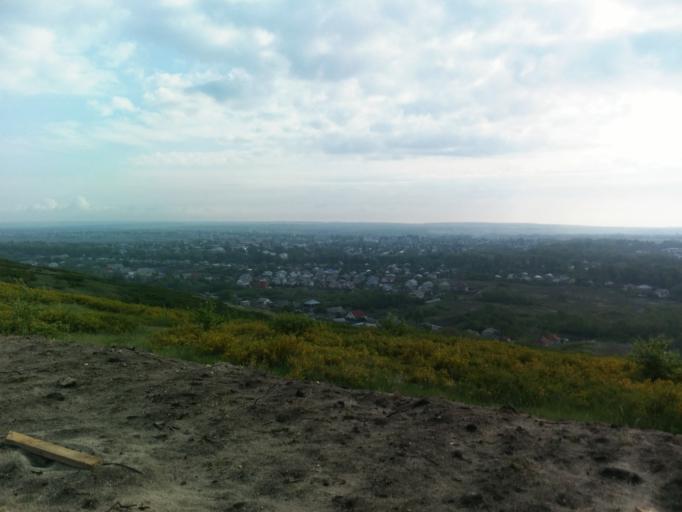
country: RU
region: Voronezj
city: Kalach
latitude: 50.4138
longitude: 41.0033
